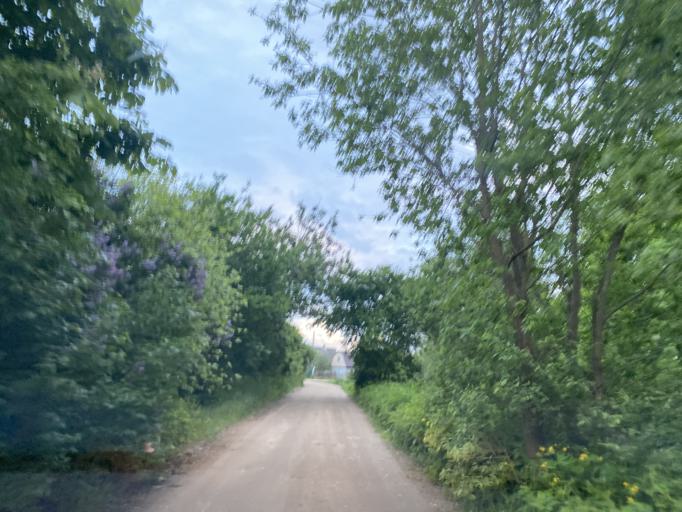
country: BY
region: Minsk
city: Rudzyensk
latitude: 53.6066
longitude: 27.7918
